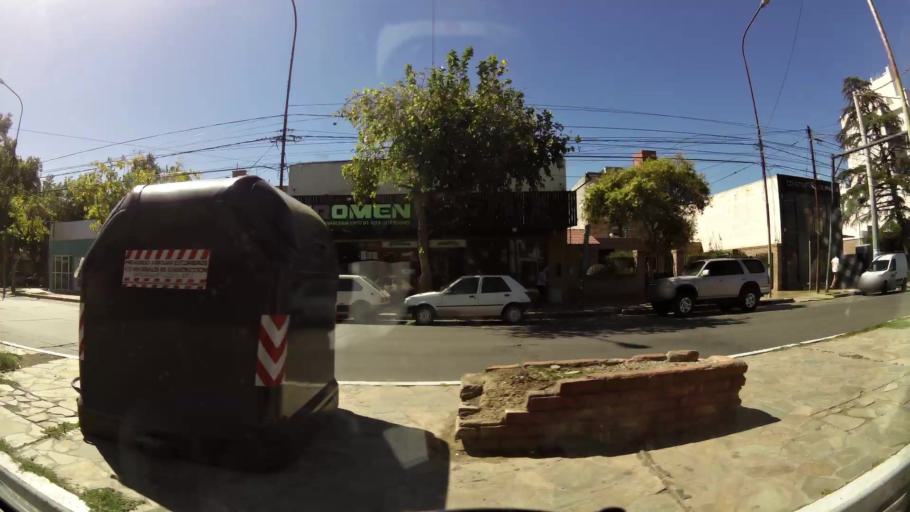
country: AR
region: San Juan
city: San Juan
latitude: -31.5379
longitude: -68.5402
